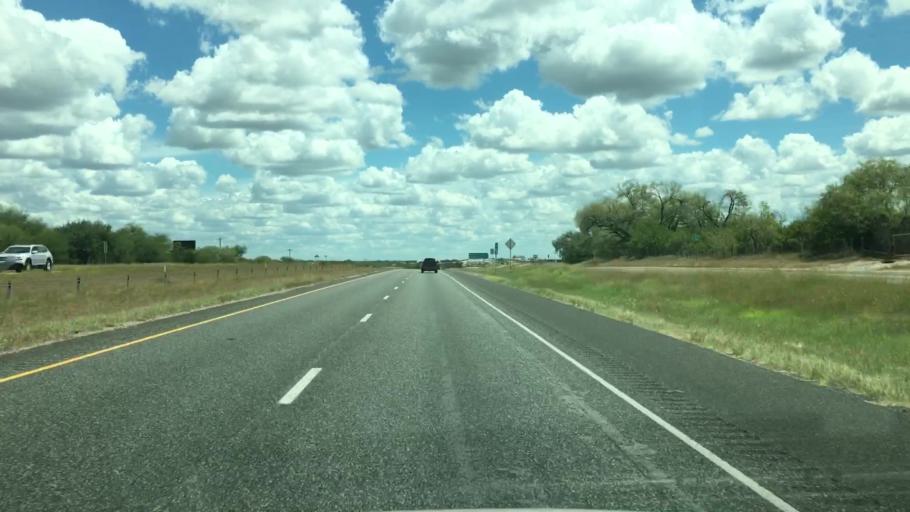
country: US
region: Texas
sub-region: Atascosa County
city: Pleasanton
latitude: 28.9010
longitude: -98.4221
